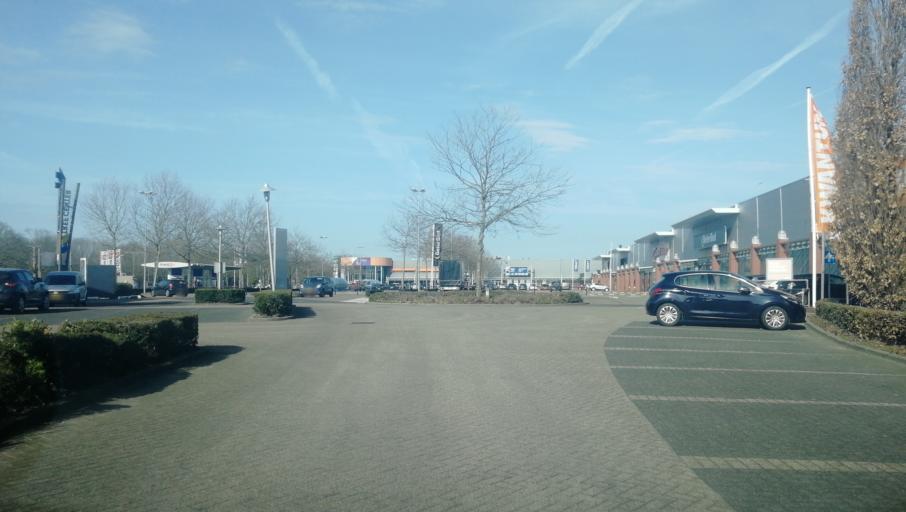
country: NL
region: Limburg
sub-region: Gemeente Venlo
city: Venlo
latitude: 51.3829
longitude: 6.1838
